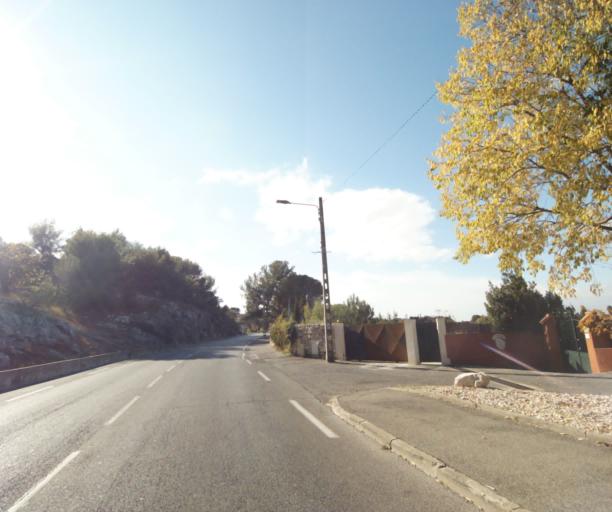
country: FR
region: Provence-Alpes-Cote d'Azur
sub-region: Departement des Bouches-du-Rhone
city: Allauch
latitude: 43.3412
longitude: 5.4856
